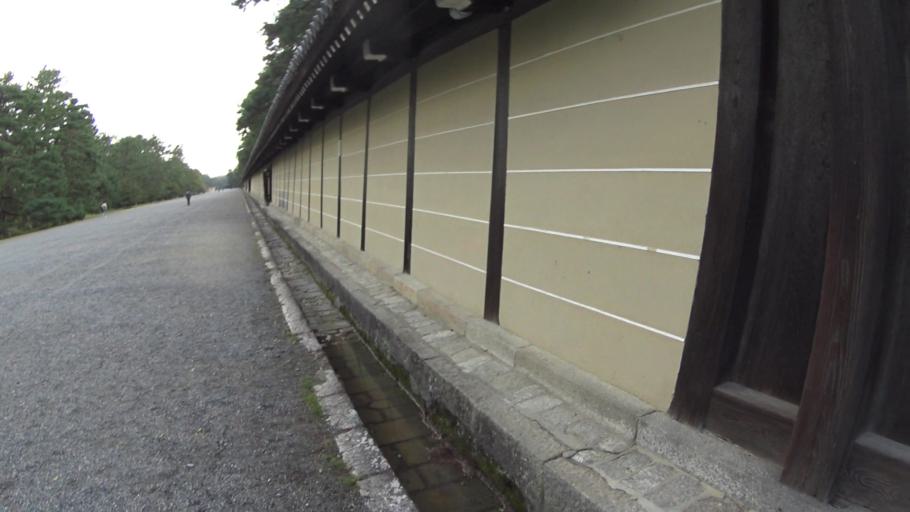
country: JP
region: Kyoto
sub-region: Kyoto-shi
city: Kamigyo-ku
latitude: 35.0271
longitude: 135.7637
